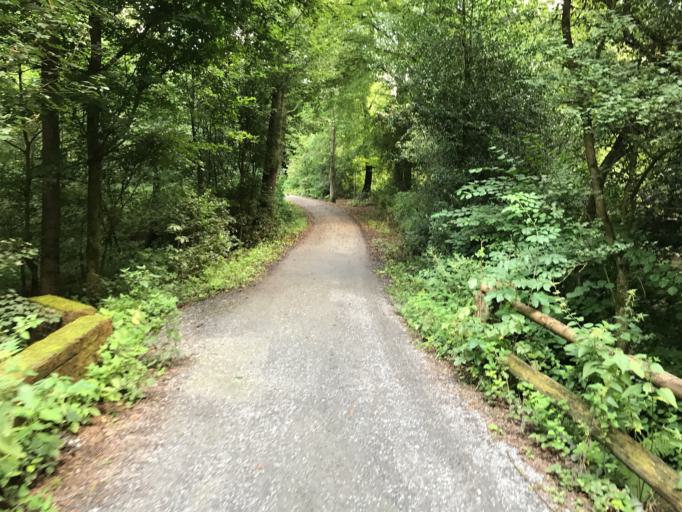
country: DE
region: North Rhine-Westphalia
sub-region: Regierungsbezirk Dusseldorf
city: Duisburg
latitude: 51.4167
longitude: 6.8071
